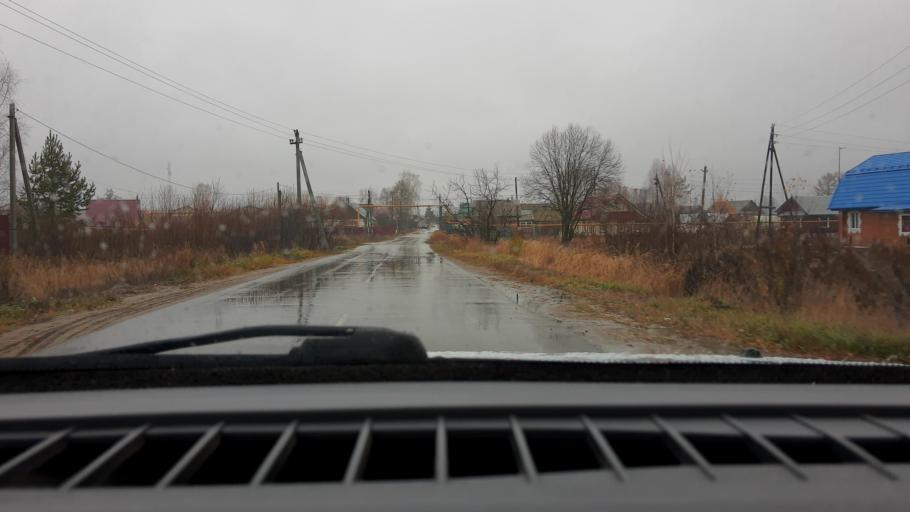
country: RU
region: Nizjnij Novgorod
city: Linda
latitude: 56.6794
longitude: 44.1953
